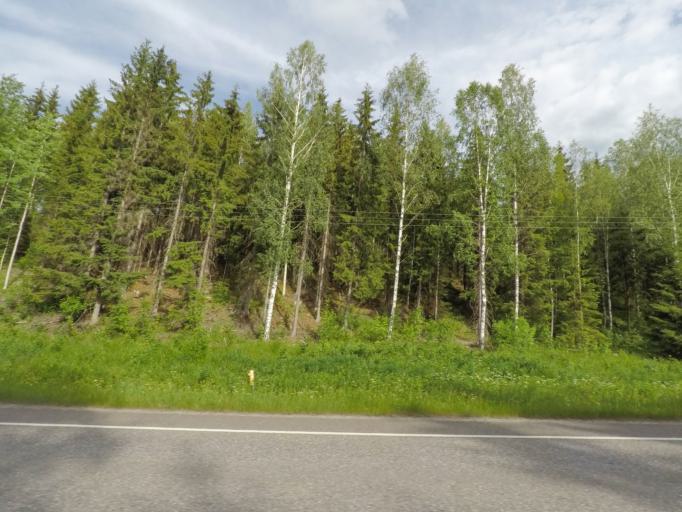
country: FI
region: Paijanne Tavastia
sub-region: Lahti
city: Hollola
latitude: 60.8741
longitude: 25.5035
